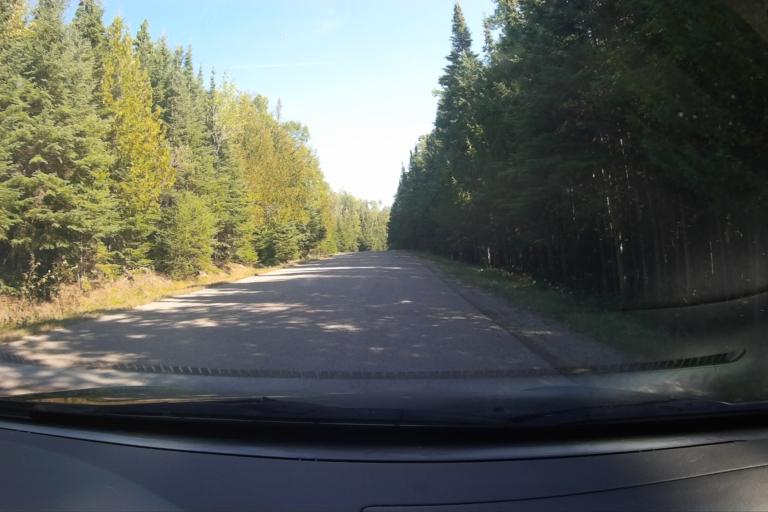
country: CA
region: Ontario
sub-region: Thunder Bay District
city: Thunder Bay
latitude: 48.3458
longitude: -88.8100
